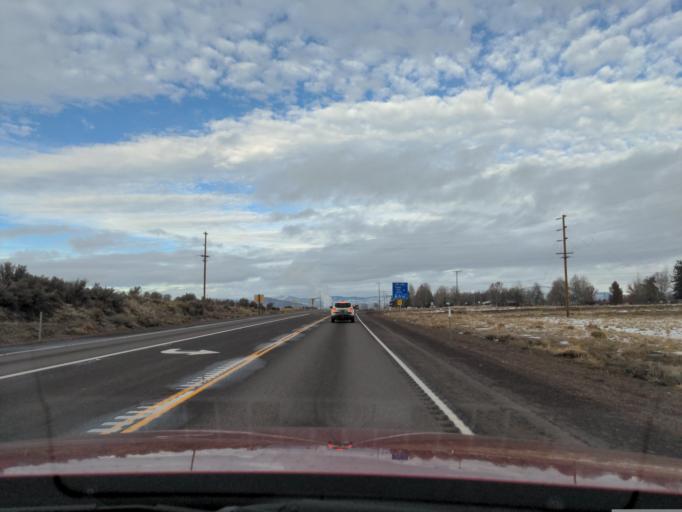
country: US
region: Oregon
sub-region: Klamath County
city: Klamath Falls
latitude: 42.1231
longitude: -121.8274
